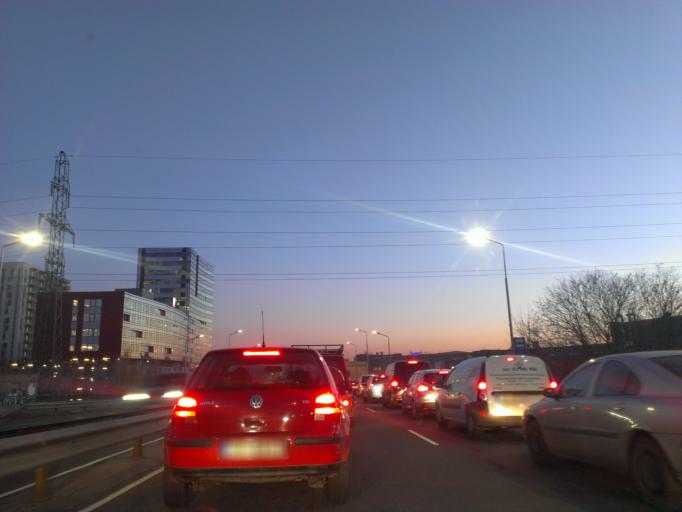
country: LV
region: Riga
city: Jaunciems
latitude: 56.9788
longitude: 24.1632
